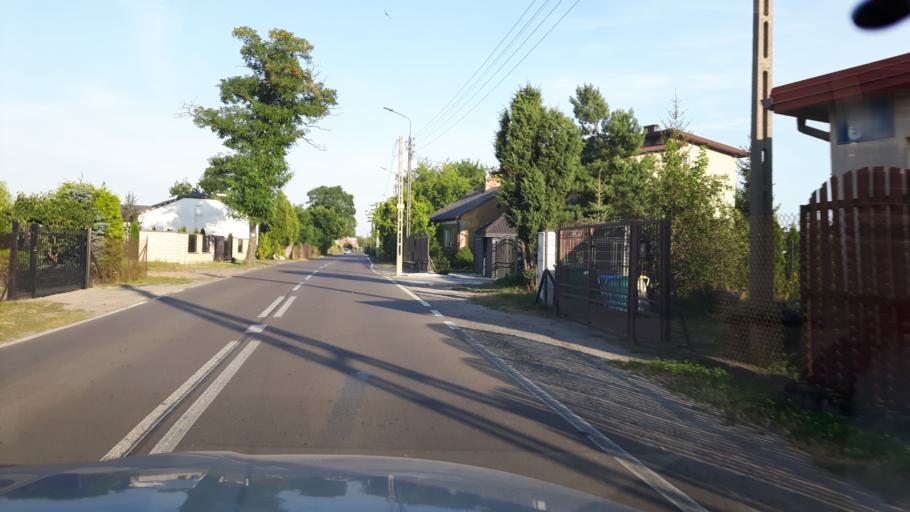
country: PL
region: Masovian Voivodeship
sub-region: Powiat wolominski
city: Slupno
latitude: 52.3632
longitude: 21.1611
